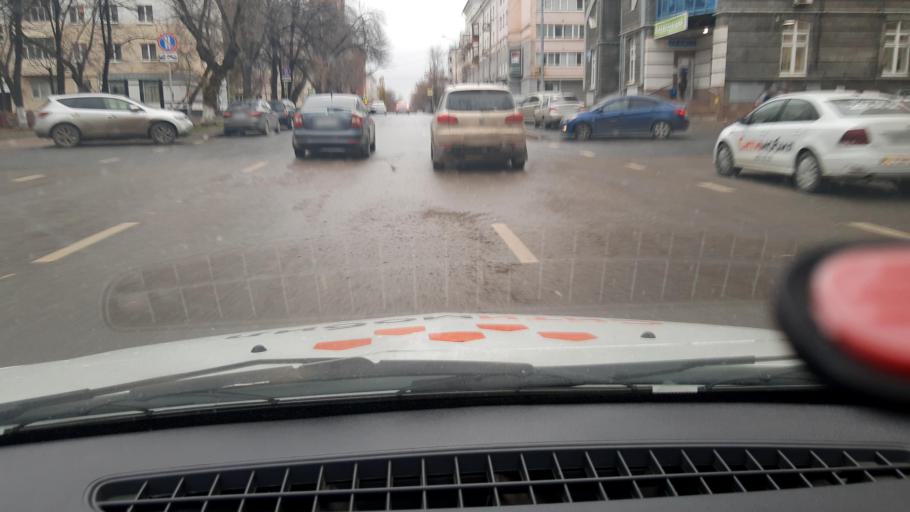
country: RU
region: Bashkortostan
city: Ufa
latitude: 54.7344
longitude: 55.9454
